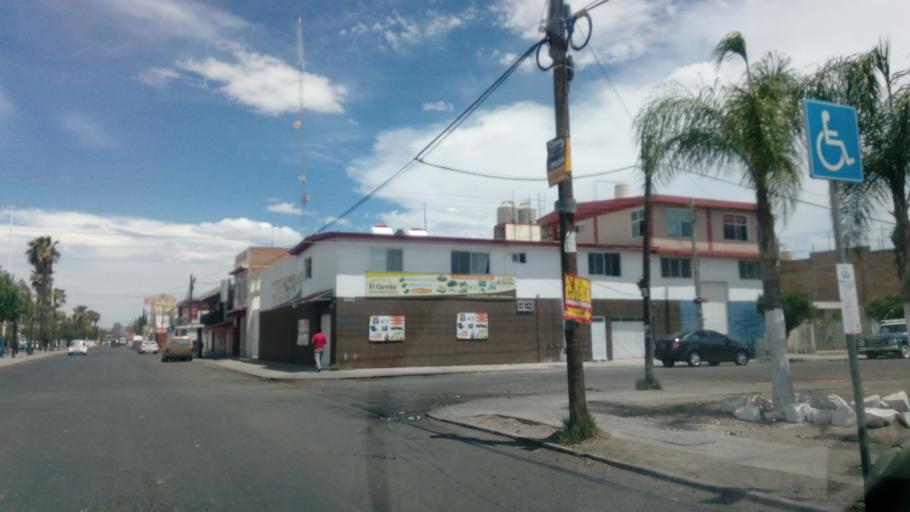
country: MX
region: Durango
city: Victoria de Durango
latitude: 23.9967
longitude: -104.6701
